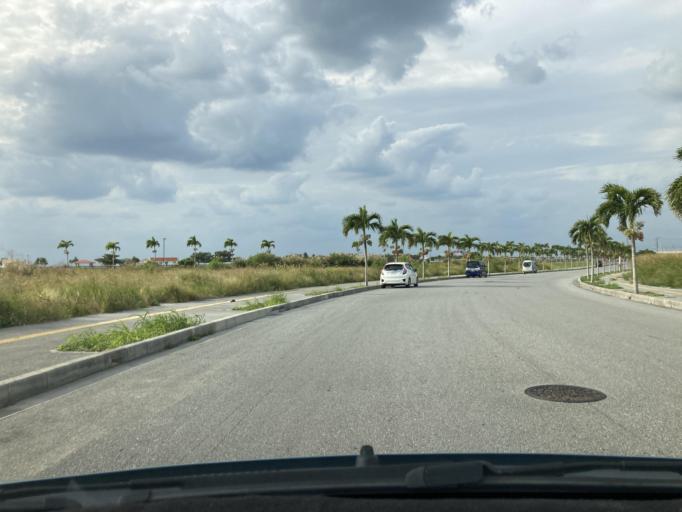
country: JP
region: Okinawa
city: Itoman
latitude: 26.1532
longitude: 127.6511
